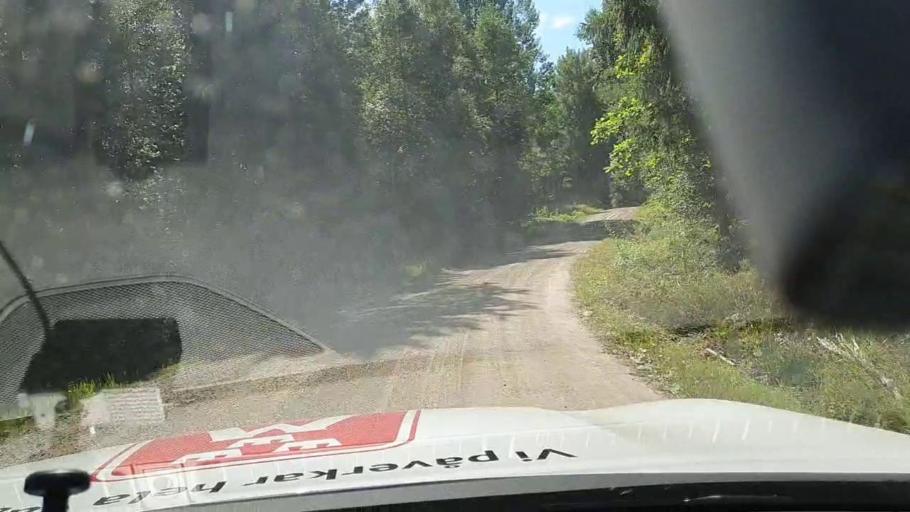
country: SE
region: Soedermanland
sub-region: Strangnas Kommun
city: Akers Styckebruk
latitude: 59.2076
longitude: 16.9187
